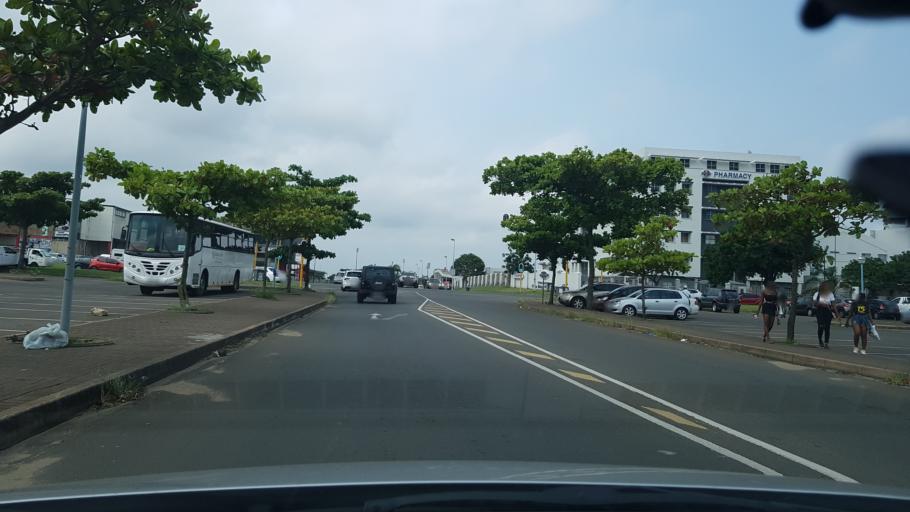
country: ZA
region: KwaZulu-Natal
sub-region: uThungulu District Municipality
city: Richards Bay
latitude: -28.7510
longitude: 32.0518
